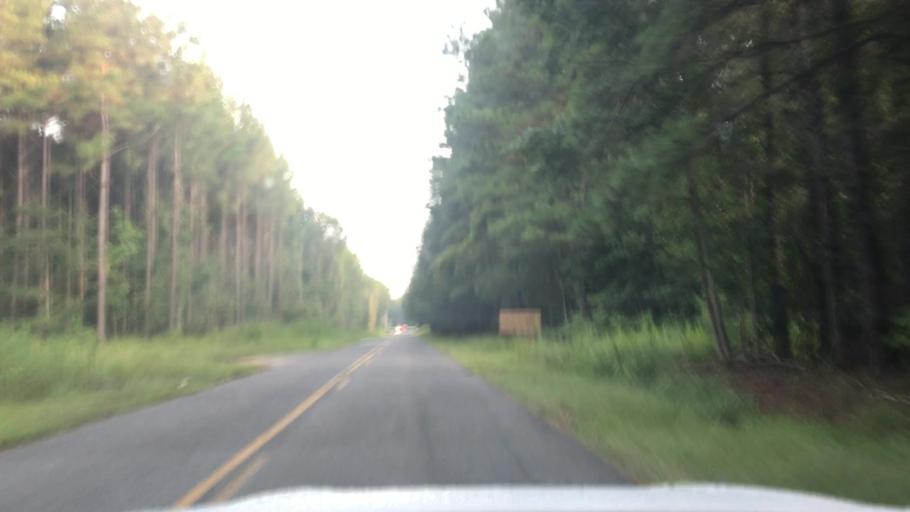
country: US
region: South Carolina
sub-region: Charleston County
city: Shell Point
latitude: 32.8160
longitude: -80.0896
